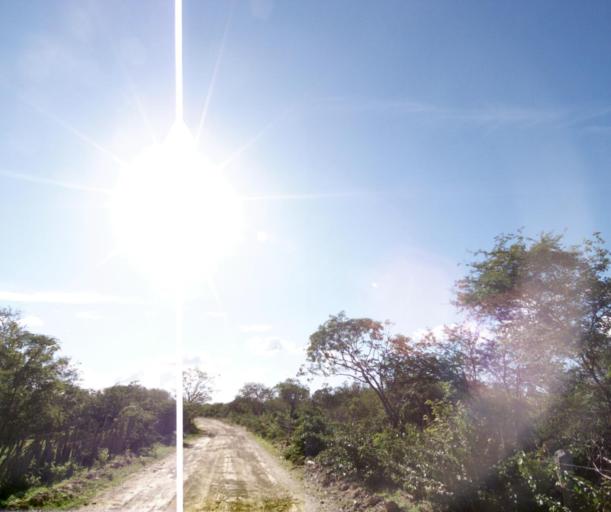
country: BR
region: Bahia
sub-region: Tanhacu
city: Tanhacu
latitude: -14.1878
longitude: -40.9575
